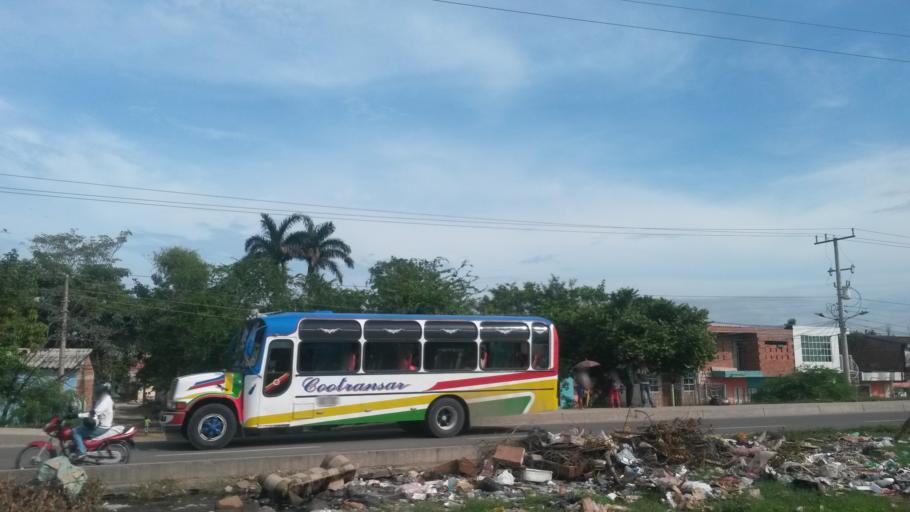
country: CO
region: Bolivar
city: Cartagena
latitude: 10.4046
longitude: -75.4555
